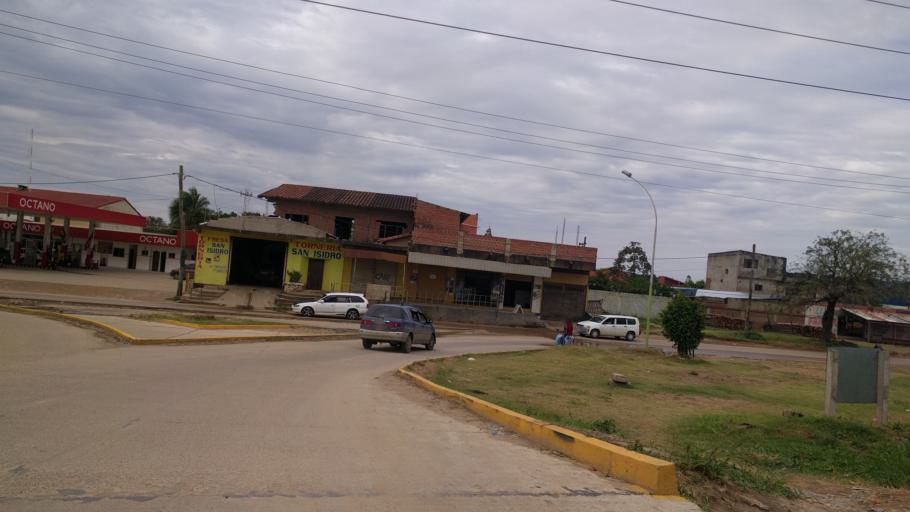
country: BO
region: Santa Cruz
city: Santa Cruz de la Sierra
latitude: -17.8427
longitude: -63.1733
